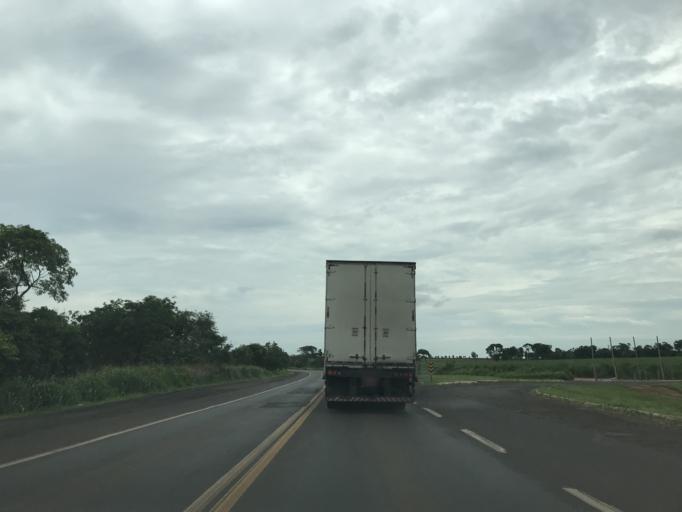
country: BR
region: Minas Gerais
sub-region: Frutal
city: Frutal
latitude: -20.1850
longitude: -49.1170
